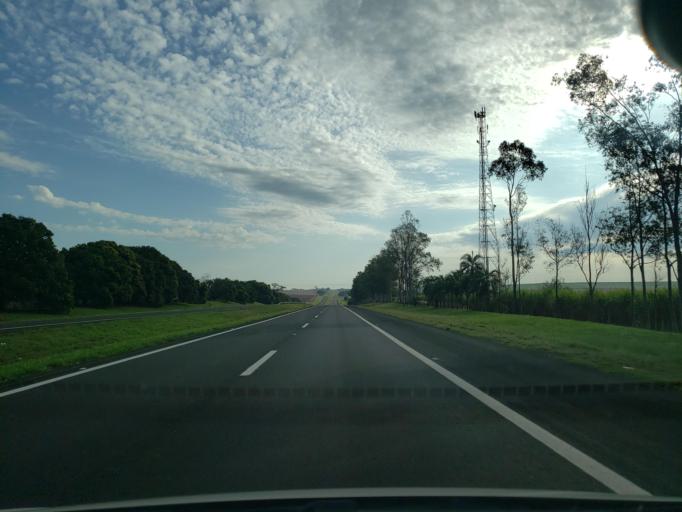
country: BR
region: Sao Paulo
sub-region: Valparaiso
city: Valparaiso
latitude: -21.2066
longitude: -50.7636
